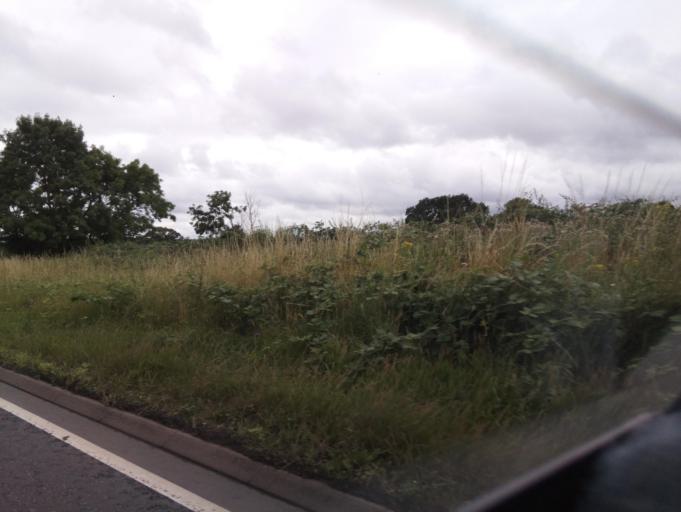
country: GB
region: England
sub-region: Worcestershire
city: Fernhill Heath
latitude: 52.2358
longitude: -2.1729
